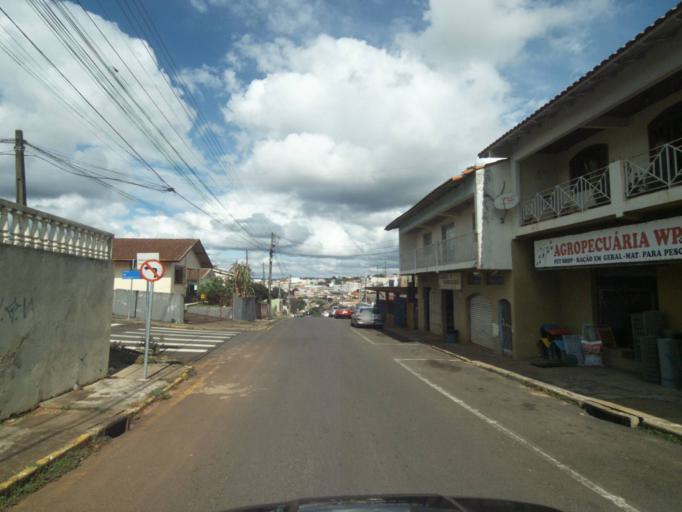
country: BR
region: Parana
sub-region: Telemaco Borba
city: Telemaco Borba
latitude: -24.3241
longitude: -50.6299
